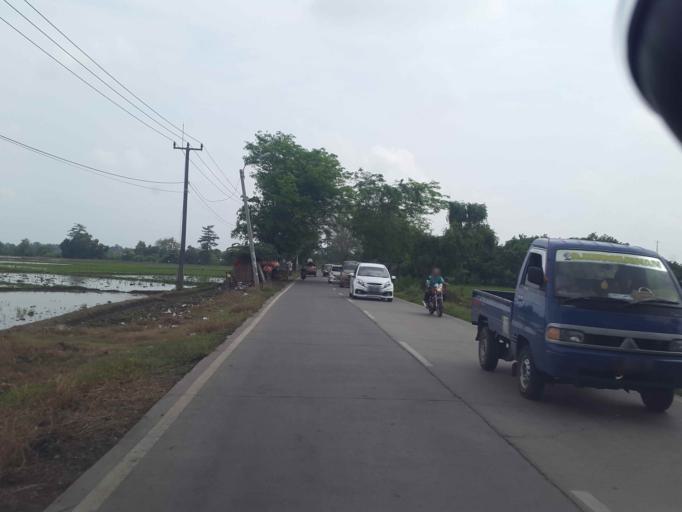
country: ID
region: West Java
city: Rengasdengklok
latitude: -6.2892
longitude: 107.3734
